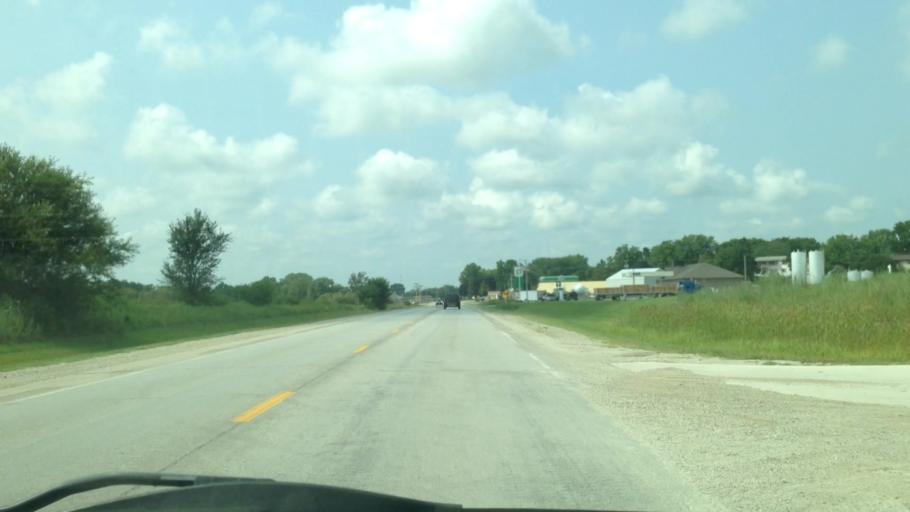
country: US
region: Iowa
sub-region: Benton County
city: Walford
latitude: 41.8823
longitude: -91.8279
